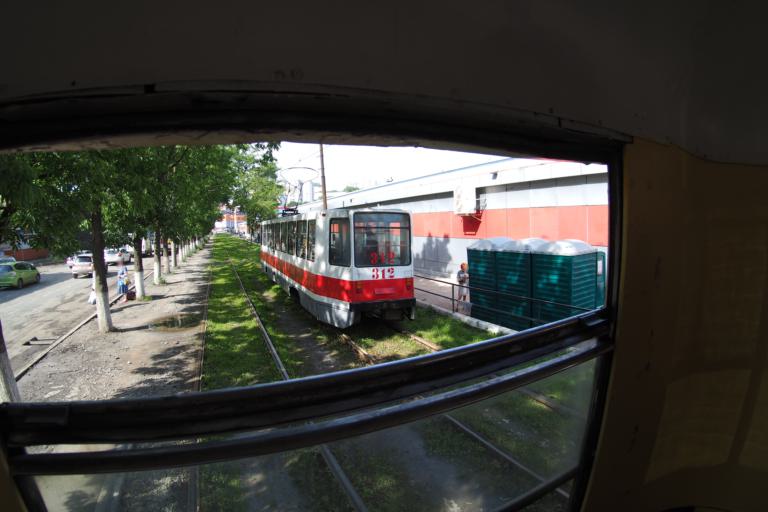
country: RU
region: Primorskiy
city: Vladivostok
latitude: 43.1055
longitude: 131.9385
